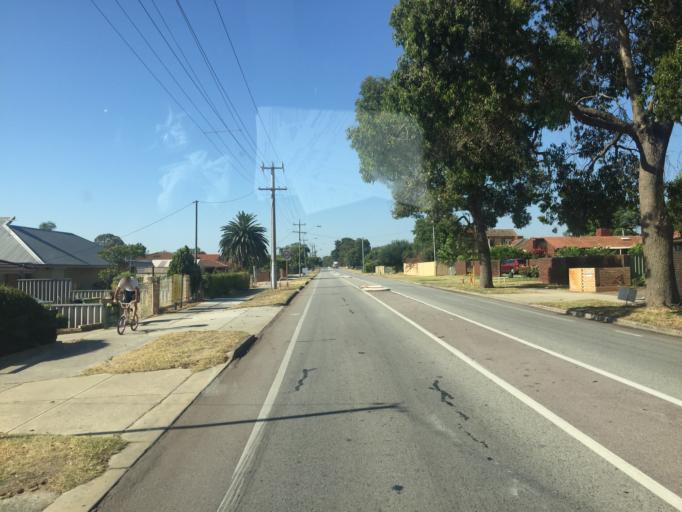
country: AU
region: Western Australia
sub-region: Gosnells
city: Maddington
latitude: -32.0395
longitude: 115.9820
